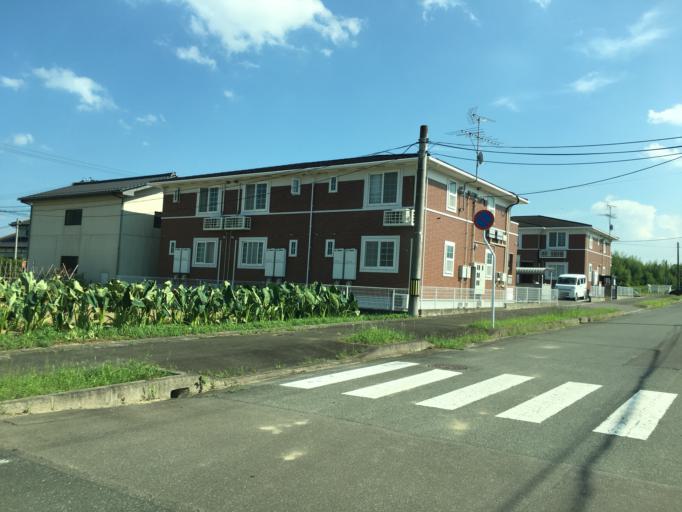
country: JP
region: Miyagi
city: Marumori
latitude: 37.8039
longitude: 140.9369
